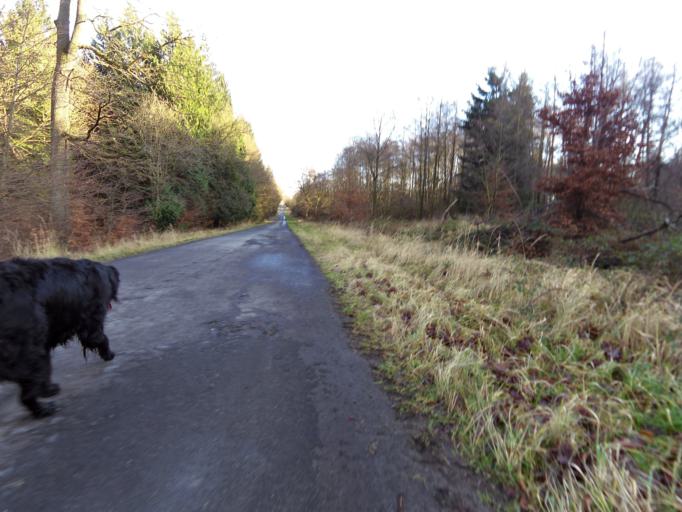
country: DE
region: Hesse
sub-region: Regierungsbezirk Kassel
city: Fuldatal
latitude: 51.4467
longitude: 9.5758
